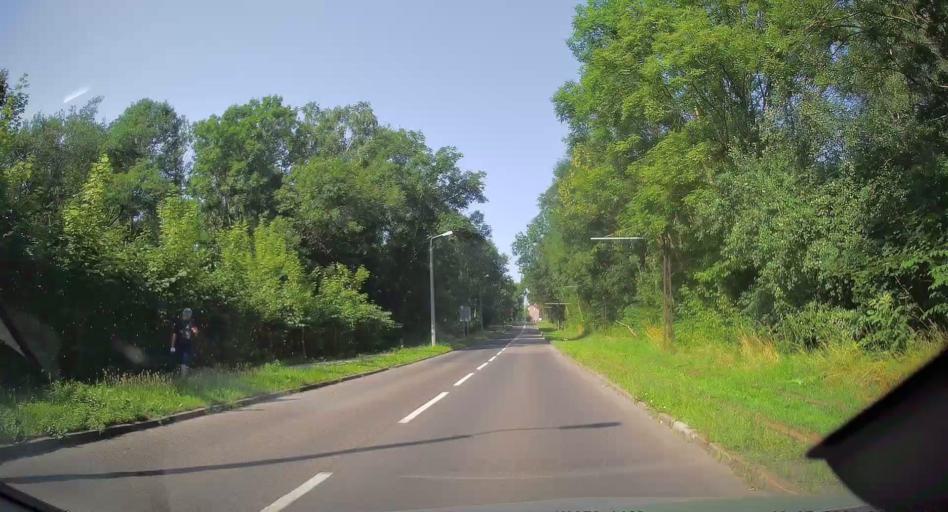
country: PL
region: Silesian Voivodeship
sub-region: Ruda Slaska
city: Ruda Slaska
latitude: 50.2731
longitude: 18.8887
